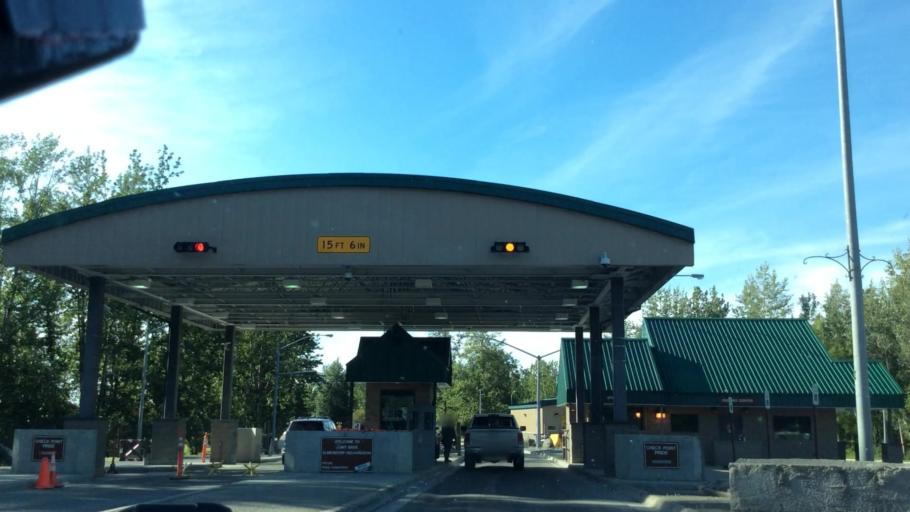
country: US
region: Alaska
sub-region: Anchorage Municipality
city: Elmendorf Air Force Base
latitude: 61.2569
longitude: -149.6631
